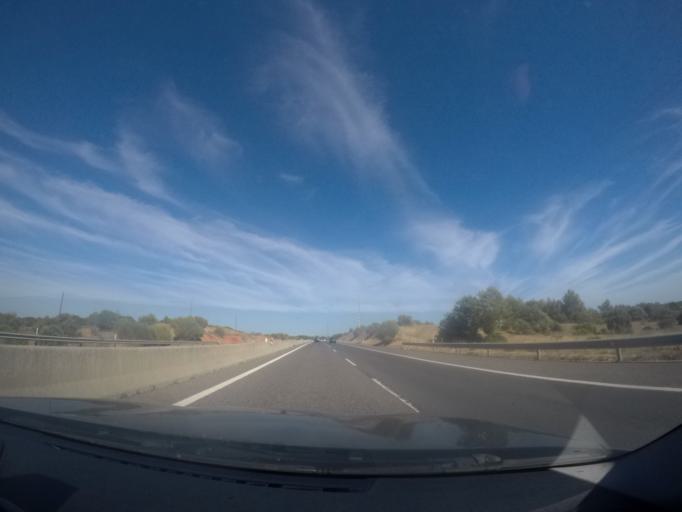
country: PT
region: Faro
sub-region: Lagoa
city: Estombar
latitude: 37.1587
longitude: -8.4935
